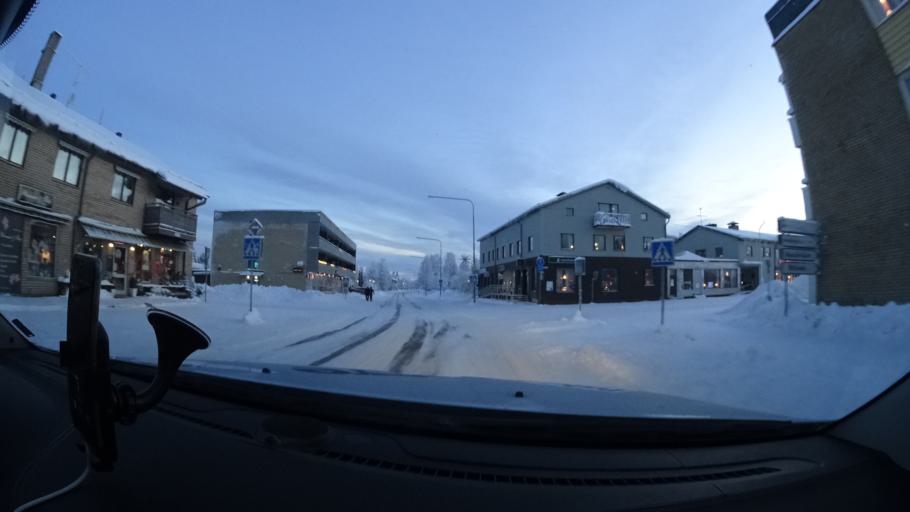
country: SE
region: Vaesterbotten
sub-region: Norsjo Kommun
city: Norsjoe
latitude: 64.9123
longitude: 19.4811
